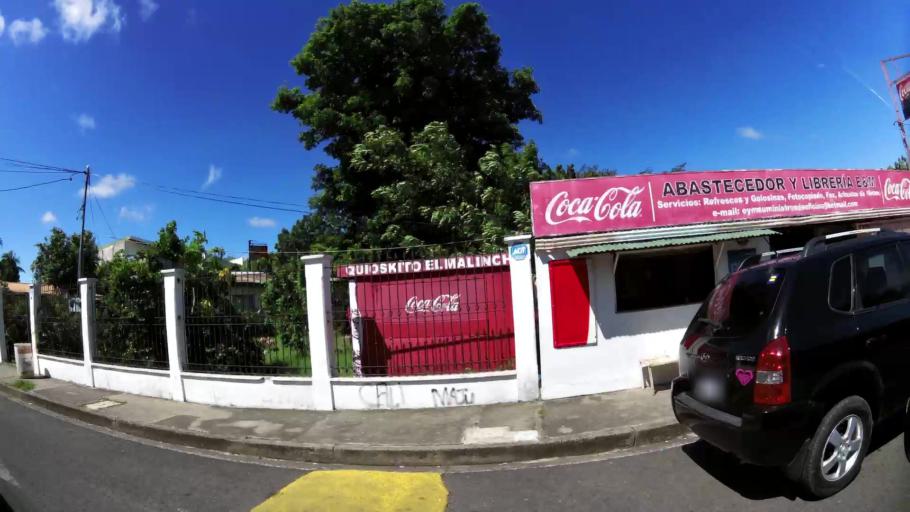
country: CR
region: Guanacaste
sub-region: Canton de Canas
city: Canas
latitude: 10.4286
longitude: -85.0871
